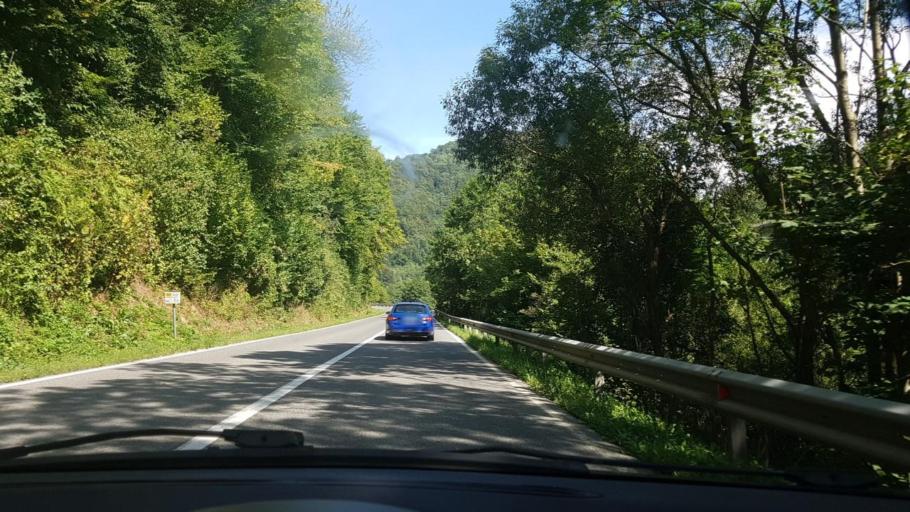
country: SI
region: Vransko
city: Vransko
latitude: 46.2188
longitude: 14.9331
